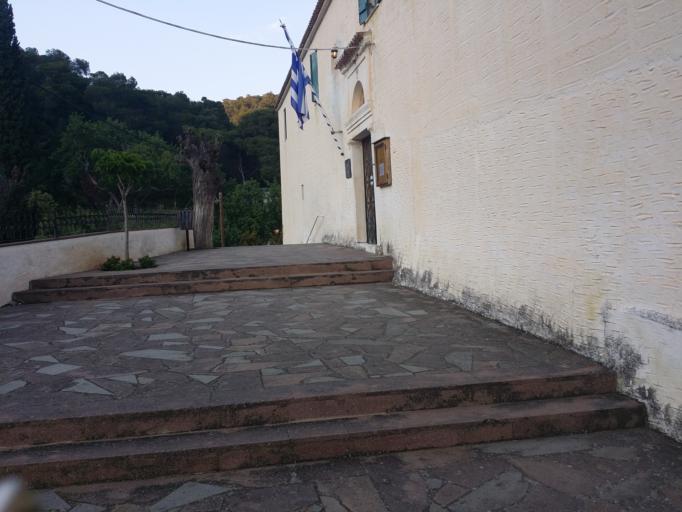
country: GR
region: Attica
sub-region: Nomos Piraios
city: Poros
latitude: 37.5067
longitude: 23.4858
